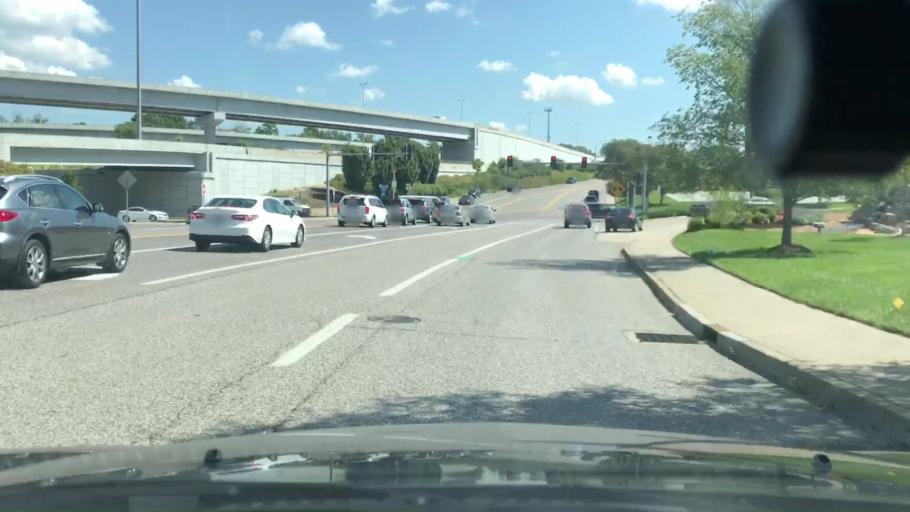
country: US
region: Missouri
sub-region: Saint Louis County
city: Brentwood
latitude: 38.6288
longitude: -90.3445
